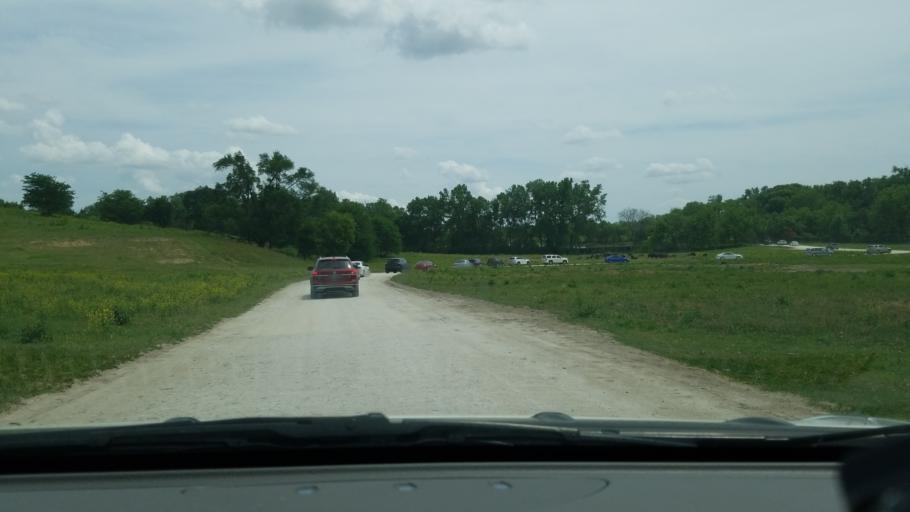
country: US
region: Nebraska
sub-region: Saunders County
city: Ashland
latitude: 41.0180
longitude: -96.2950
